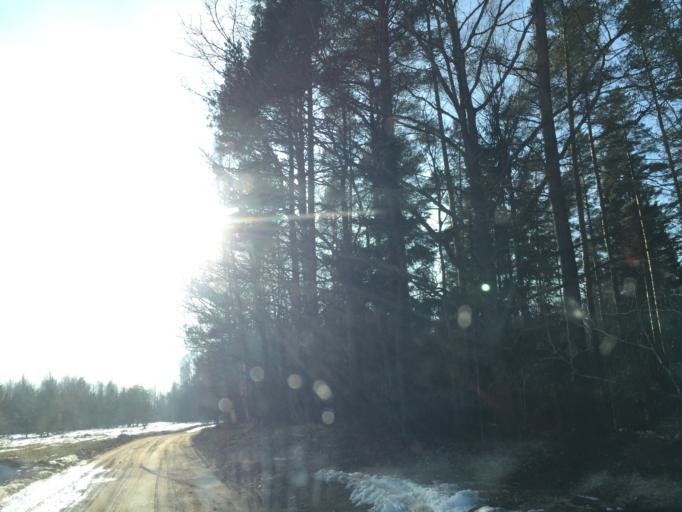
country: LV
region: Lecava
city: Iecava
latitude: 56.6785
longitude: 24.1982
